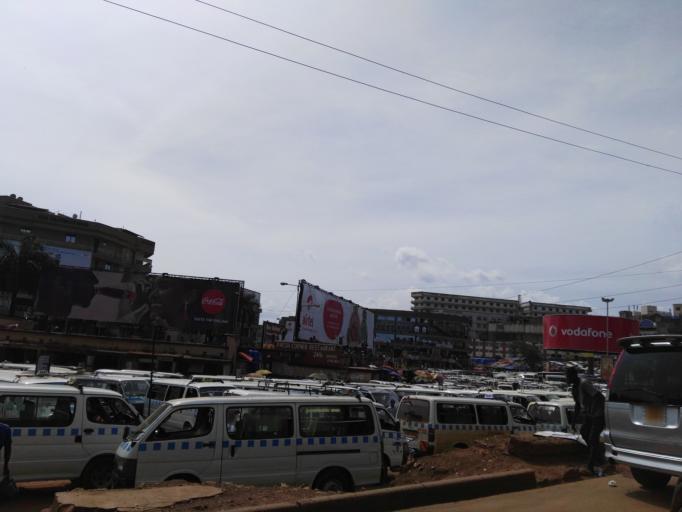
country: UG
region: Central Region
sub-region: Kampala District
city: Kampala
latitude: 0.3112
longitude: 32.5773
